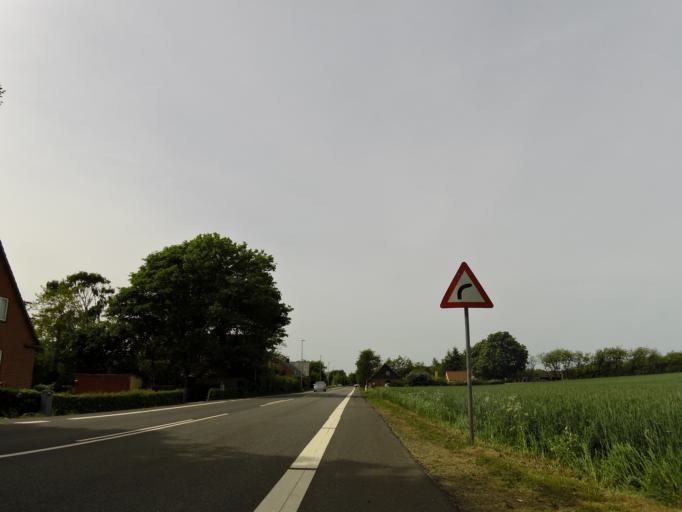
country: DK
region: Central Jutland
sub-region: Holstebro Kommune
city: Vinderup
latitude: 56.5730
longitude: 8.8597
